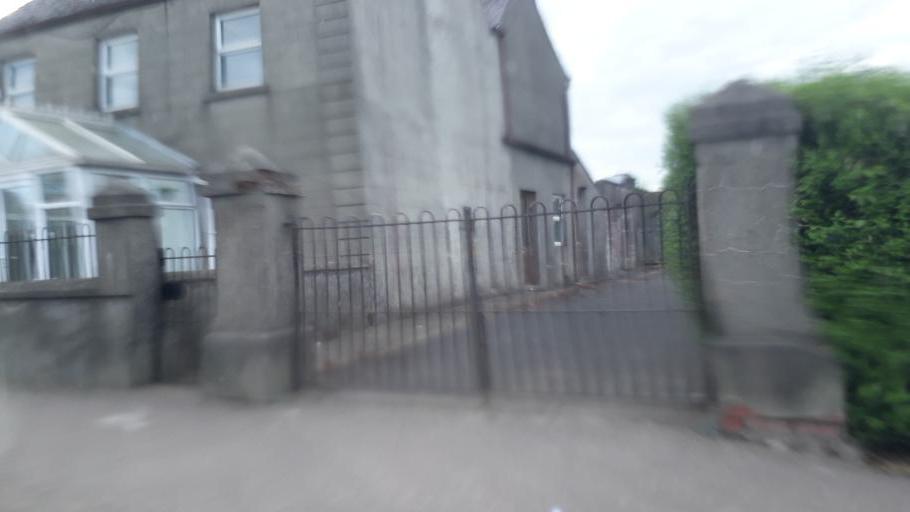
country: IE
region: Leinster
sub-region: Loch Garman
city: Gorey
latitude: 52.6773
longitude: -6.2901
